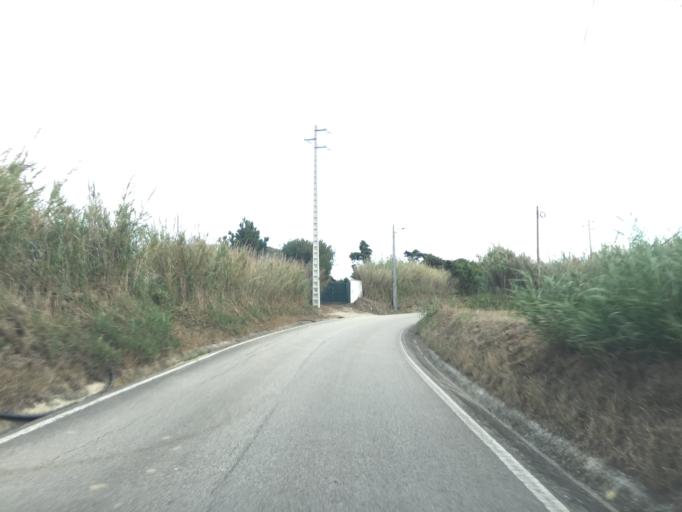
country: PT
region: Leiria
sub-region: Peniche
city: Atouguia da Baleia
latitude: 39.3450
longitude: -9.2960
